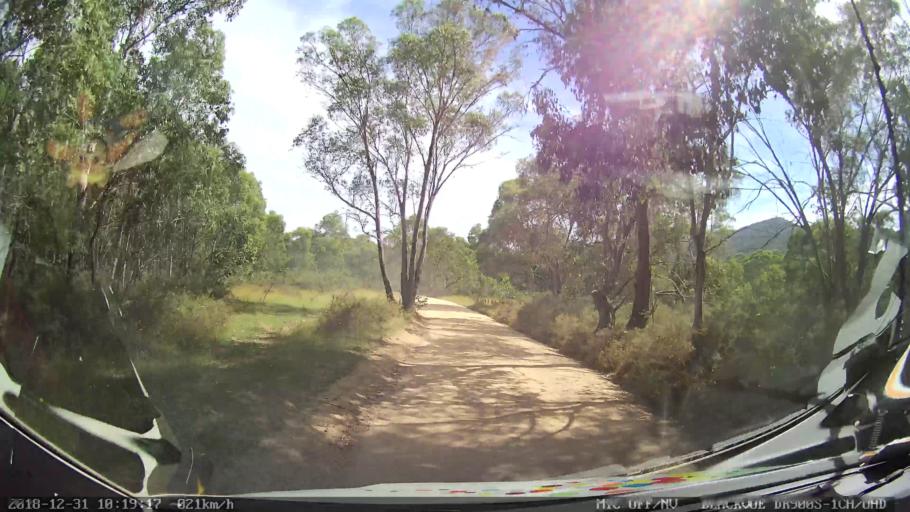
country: AU
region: New South Wales
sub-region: Snowy River
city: Jindabyne
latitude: -36.5410
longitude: 148.1346
